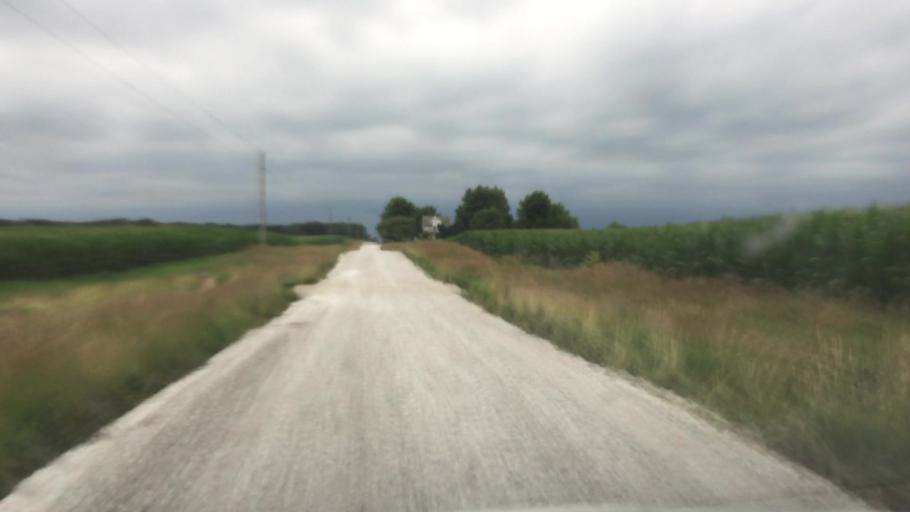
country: US
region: Illinois
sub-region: Adams County
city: Camp Point
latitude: 40.2156
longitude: -90.9665
